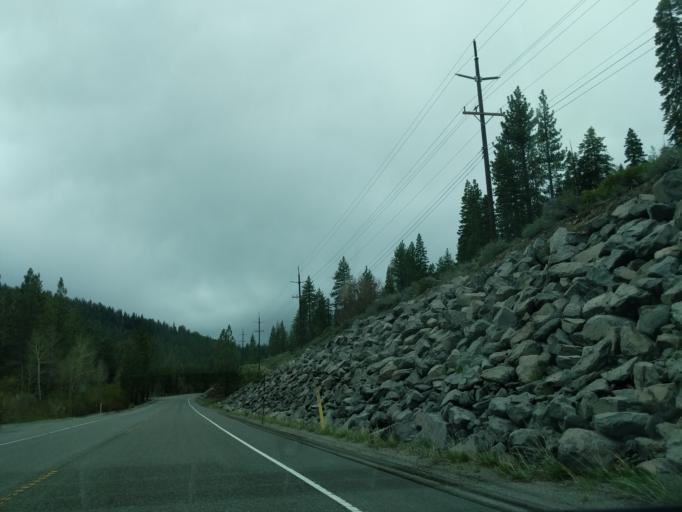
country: US
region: California
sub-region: Placer County
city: Tahoe Vista
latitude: 39.2706
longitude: -120.0891
